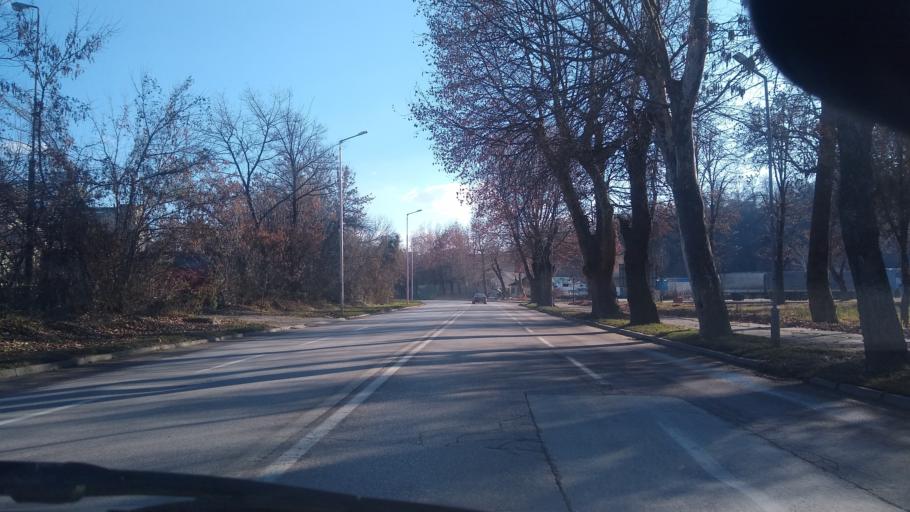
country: MK
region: Bitola
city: Bitola
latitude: 41.0178
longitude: 21.3421
